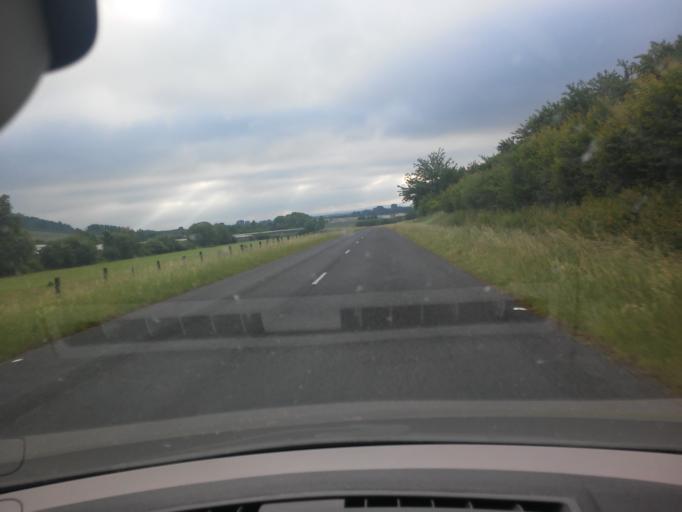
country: FR
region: Lorraine
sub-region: Departement de la Meuse
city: Vigneulles-les-Hattonchatel
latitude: 48.9672
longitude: 5.6807
